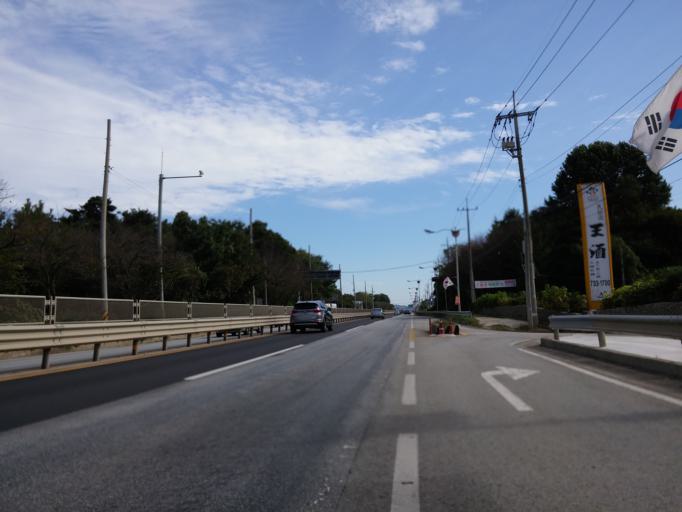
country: KR
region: Chungcheongnam-do
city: Nonsan
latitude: 36.1827
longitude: 127.0948
